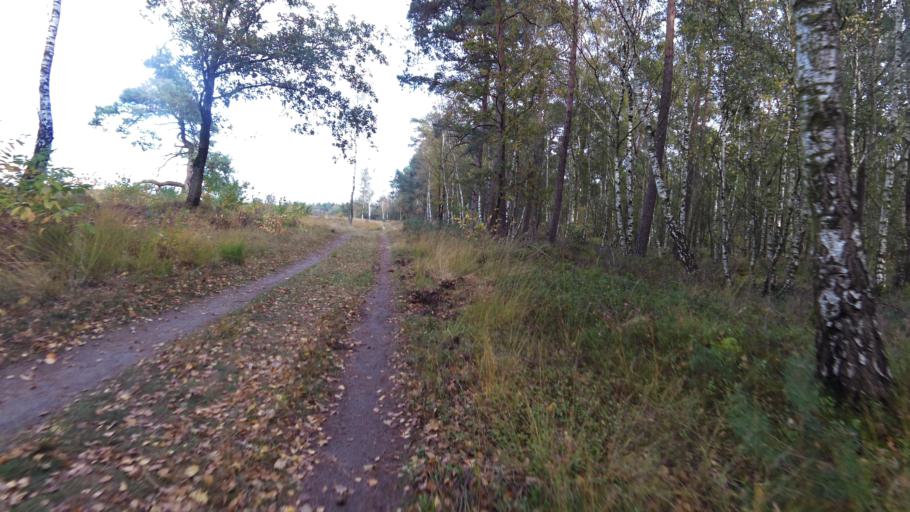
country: NL
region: Gelderland
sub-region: Gemeente Epe
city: Emst
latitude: 52.3297
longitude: 5.9091
